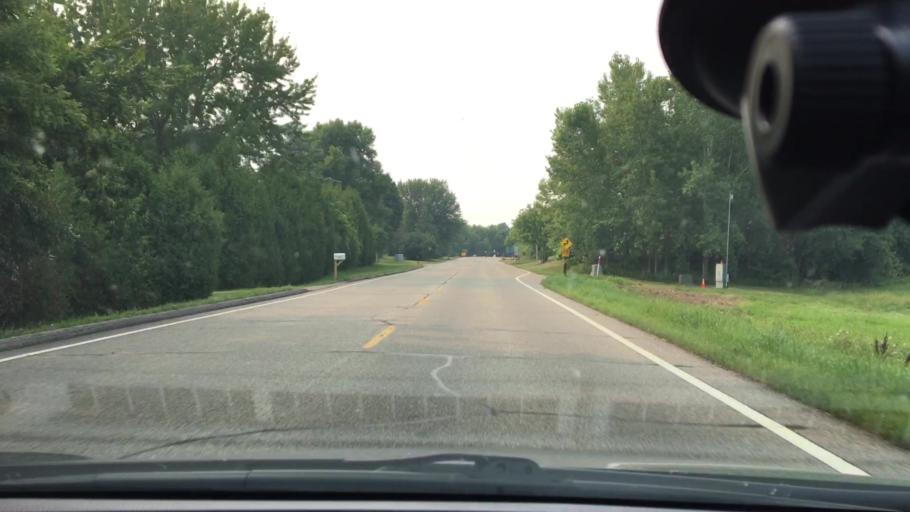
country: US
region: Minnesota
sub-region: Hennepin County
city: Dayton
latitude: 45.2384
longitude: -93.5104
